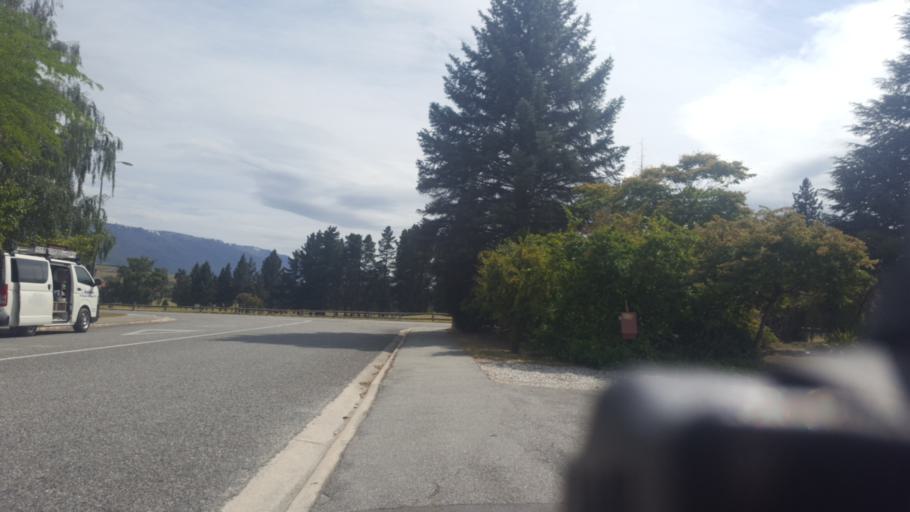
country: NZ
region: Otago
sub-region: Queenstown-Lakes District
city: Wanaka
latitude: -45.0405
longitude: 169.2021
